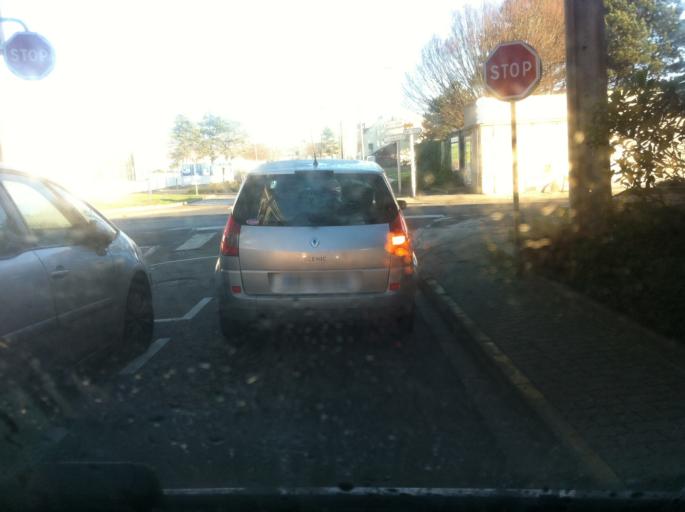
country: FR
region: Haute-Normandie
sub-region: Departement de la Seine-Maritime
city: Le Treport
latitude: 50.0585
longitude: 1.3822
